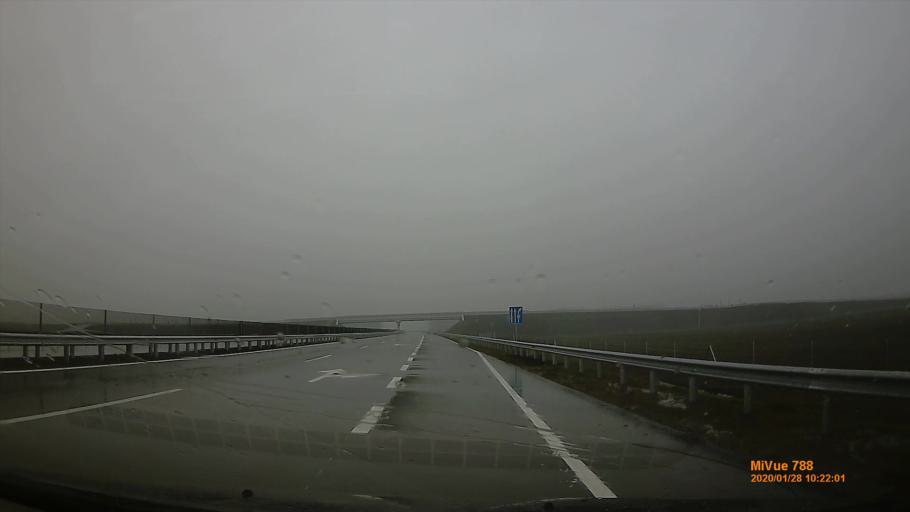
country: HU
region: Pest
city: Pilis
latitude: 47.3086
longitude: 19.5588
